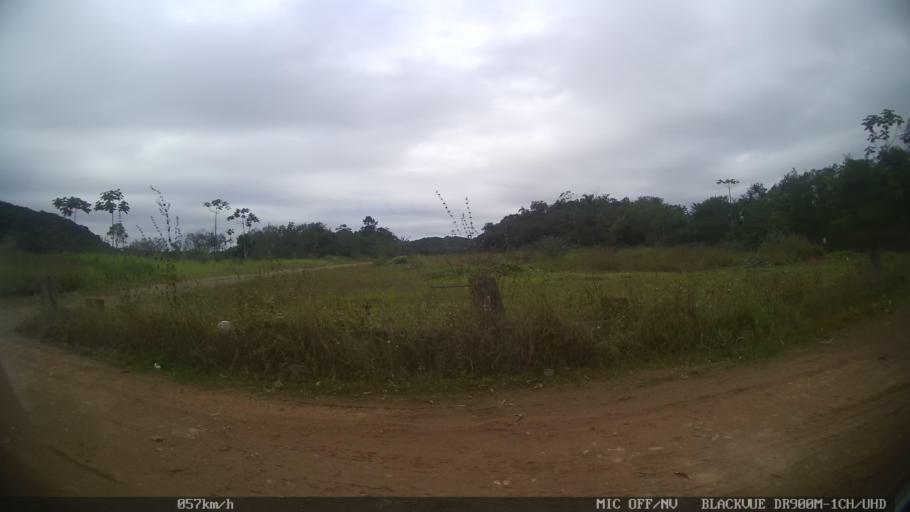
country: BR
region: Santa Catarina
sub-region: Joinville
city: Joinville
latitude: -26.2534
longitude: -48.9213
